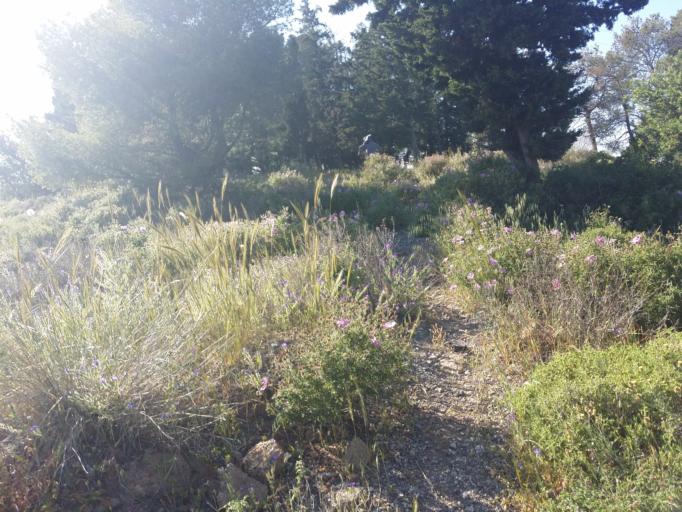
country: GR
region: Attica
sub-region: Nomos Piraios
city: Poros
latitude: 37.4996
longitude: 23.4587
